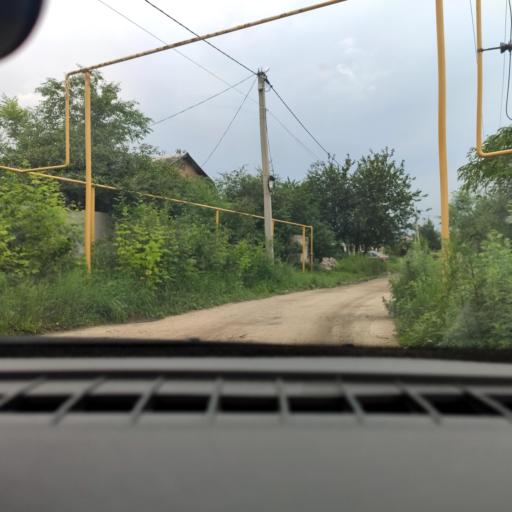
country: RU
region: Voronezj
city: Novaya Usman'
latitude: 51.6010
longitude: 39.3259
